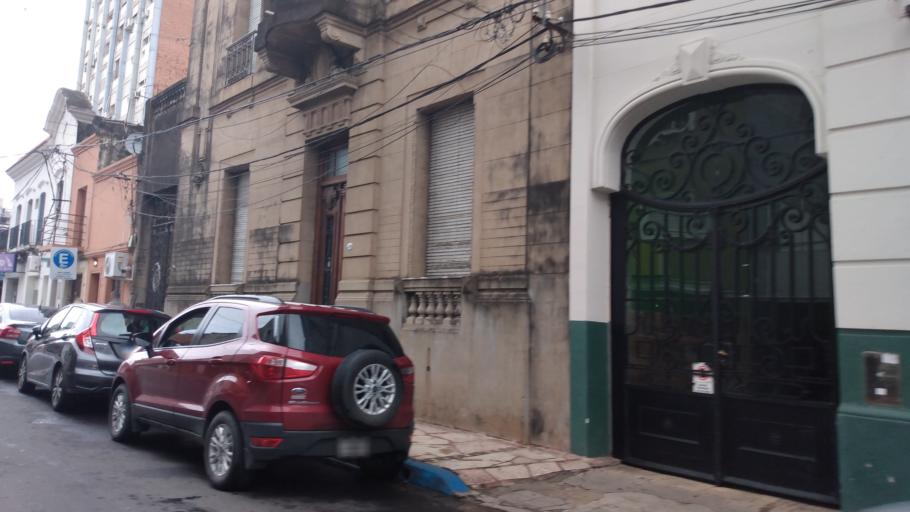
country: AR
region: Corrientes
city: Corrientes
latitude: -27.4667
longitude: -58.8338
